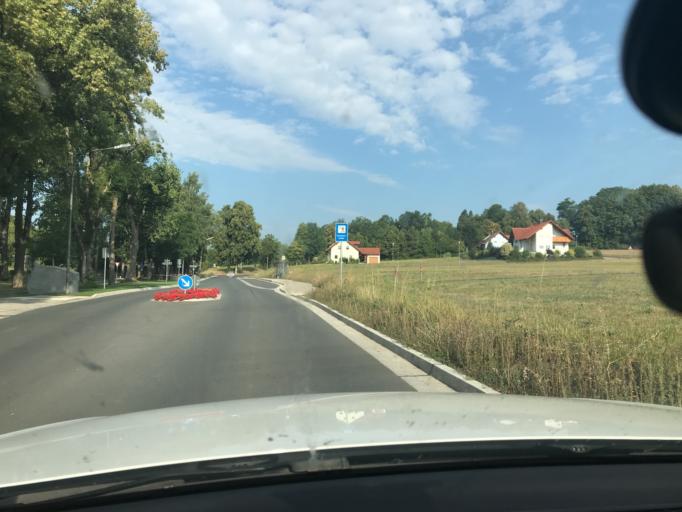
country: DE
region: Bavaria
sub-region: Upper Palatinate
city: Auerbach
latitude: 49.6962
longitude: 11.6229
